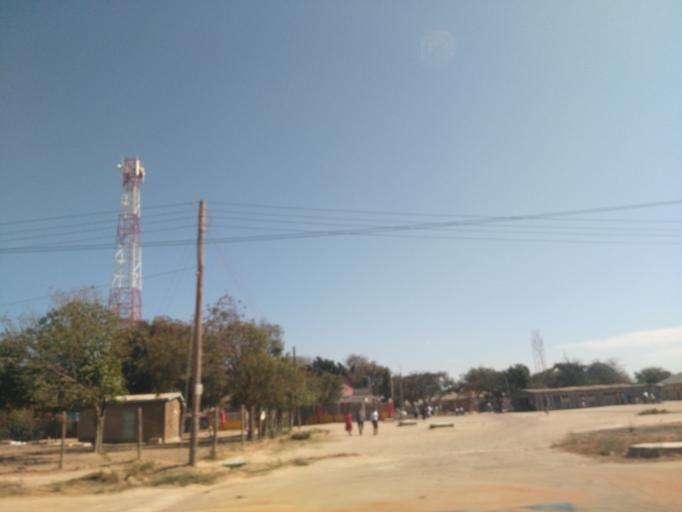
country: TZ
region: Dodoma
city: Dodoma
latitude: -6.1596
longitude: 35.7481
